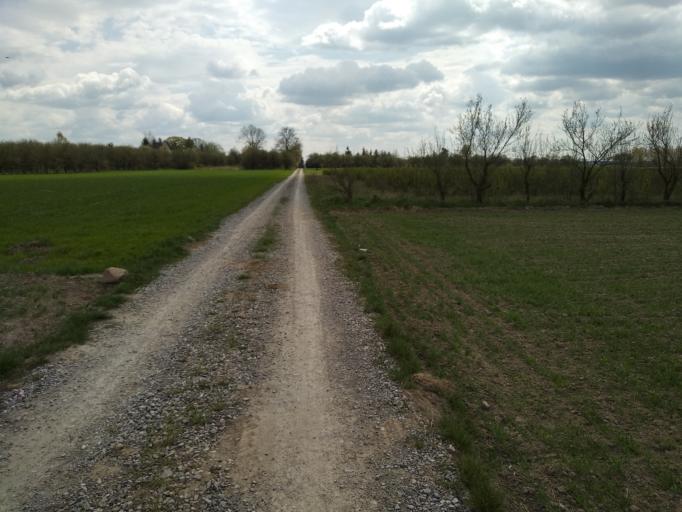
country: PL
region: Lublin Voivodeship
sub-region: Powiat lubartowski
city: Michow
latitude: 51.5001
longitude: 22.2772
